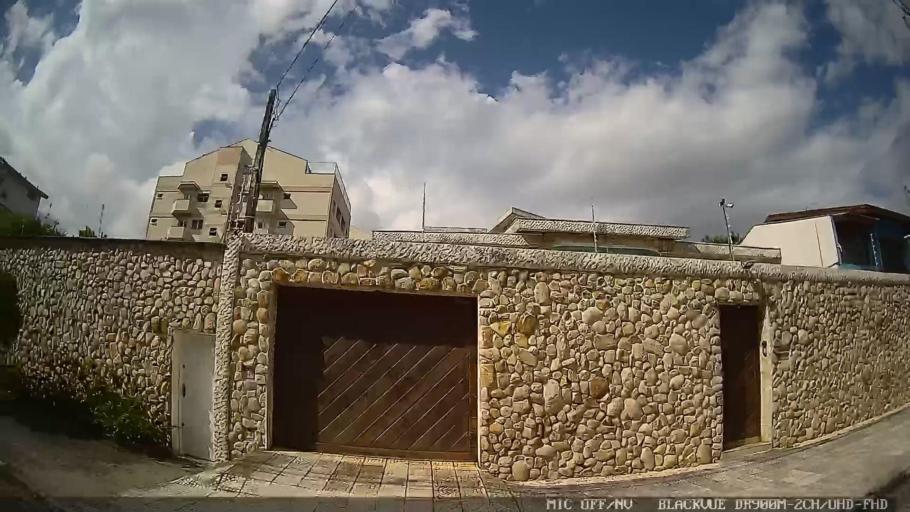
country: BR
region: Sao Paulo
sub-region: Caraguatatuba
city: Caraguatatuba
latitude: -23.6328
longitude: -45.4192
